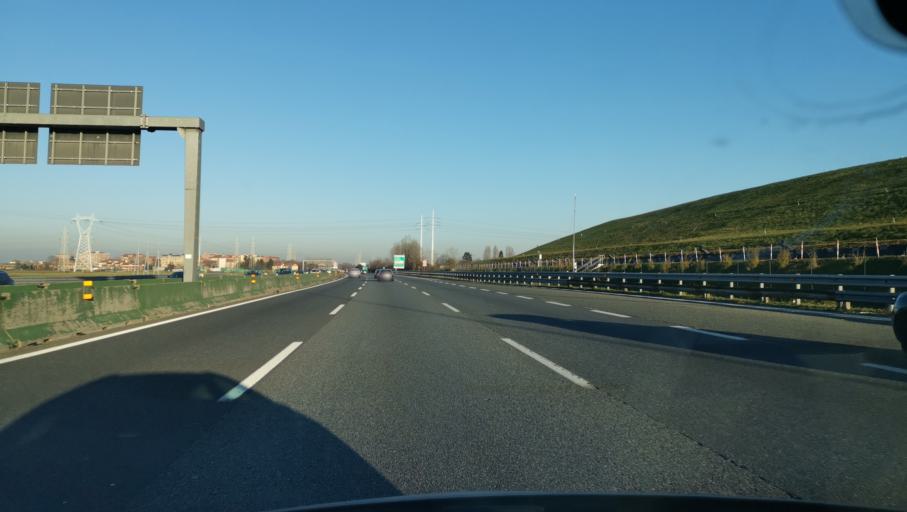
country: IT
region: Piedmont
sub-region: Provincia di Torino
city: Savonera
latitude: 45.1064
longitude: 7.6058
